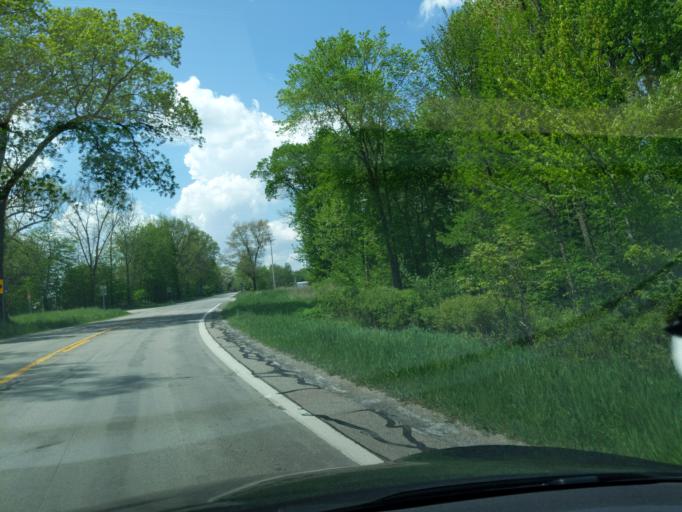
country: US
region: Michigan
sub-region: Ingham County
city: Stockbridge
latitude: 42.5014
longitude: -84.1397
